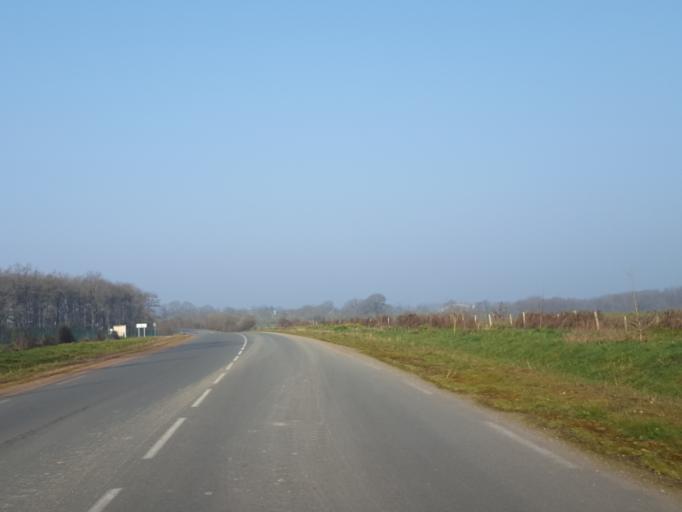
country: FR
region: Pays de la Loire
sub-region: Departement de la Vendee
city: La Chaize-le-Vicomte
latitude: 46.6695
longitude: -1.3318
